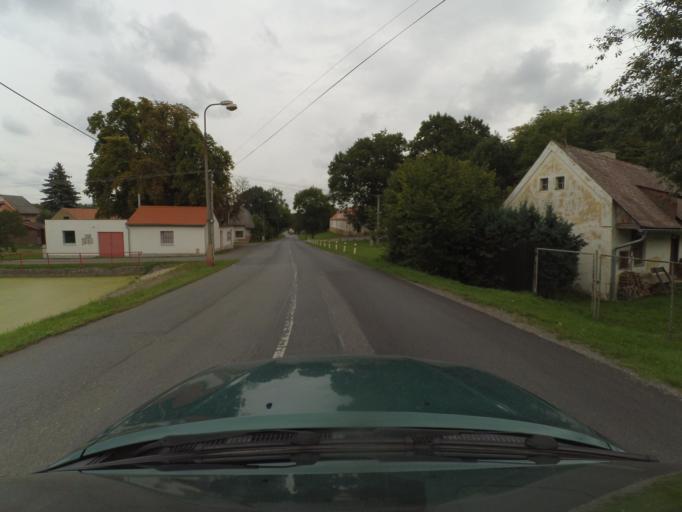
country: CZ
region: Plzensky
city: Kozlany
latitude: 50.0396
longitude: 13.6101
